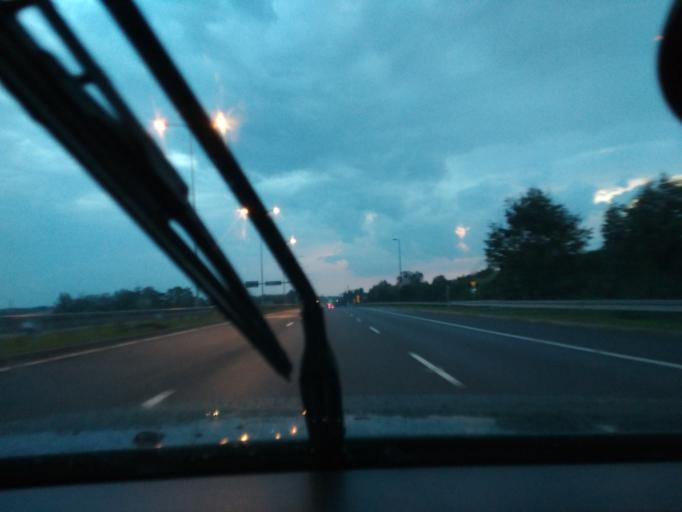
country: PL
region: Silesian Voivodeship
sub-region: Zabrze
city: Zabrze
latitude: 50.2933
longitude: 18.8014
